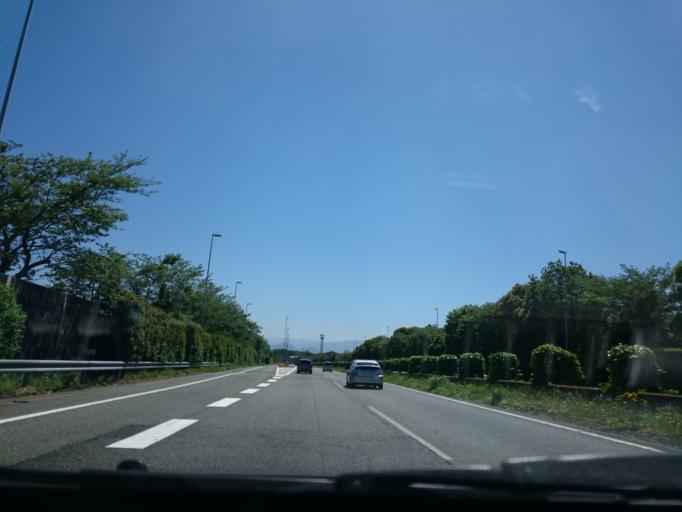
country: JP
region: Shizuoka
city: Mishima
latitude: 35.2071
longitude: 138.9027
